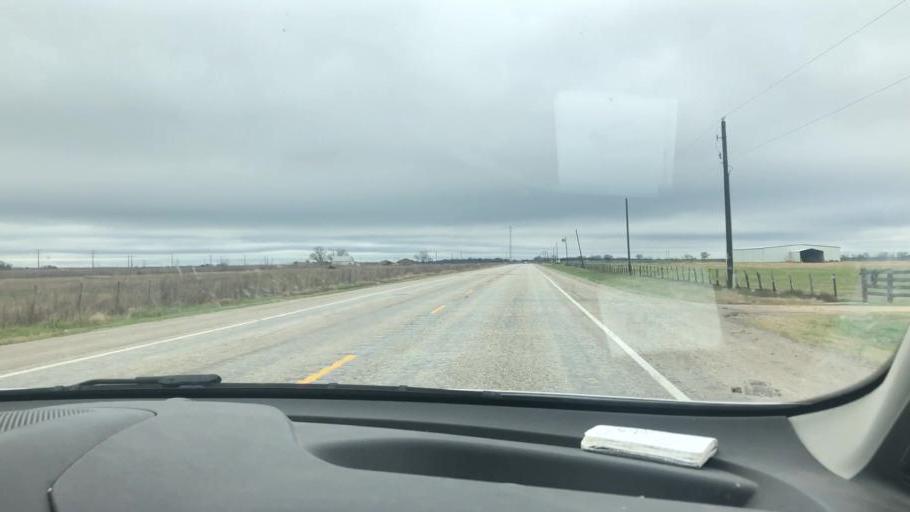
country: US
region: Texas
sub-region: Wharton County
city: Wharton
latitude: 29.2431
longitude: -96.0436
